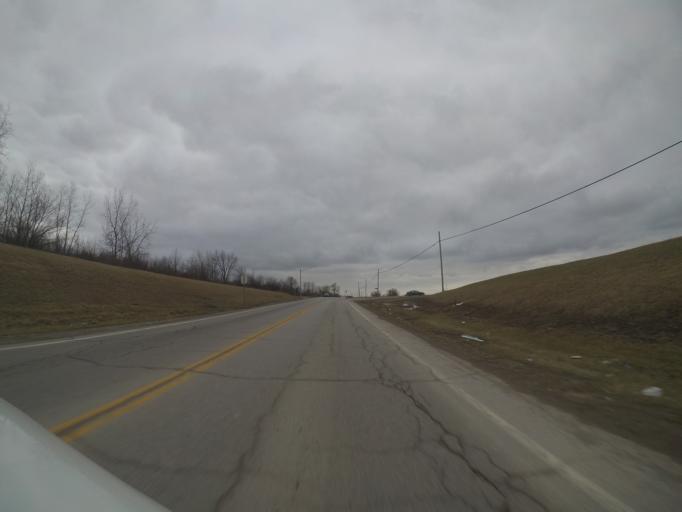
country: US
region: Ohio
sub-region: Wood County
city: Walbridge
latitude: 41.6039
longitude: -83.5123
